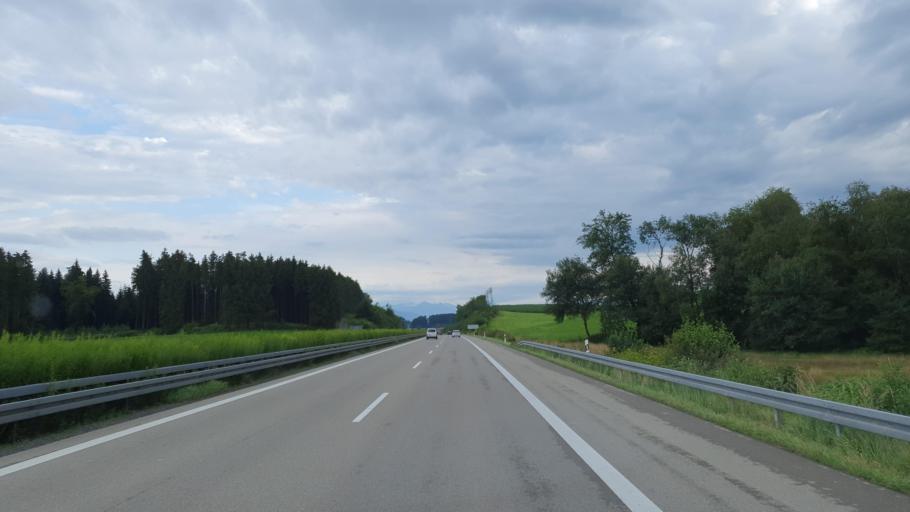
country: DE
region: Bavaria
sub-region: Swabia
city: Weissensberg
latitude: 47.6128
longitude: 9.7345
